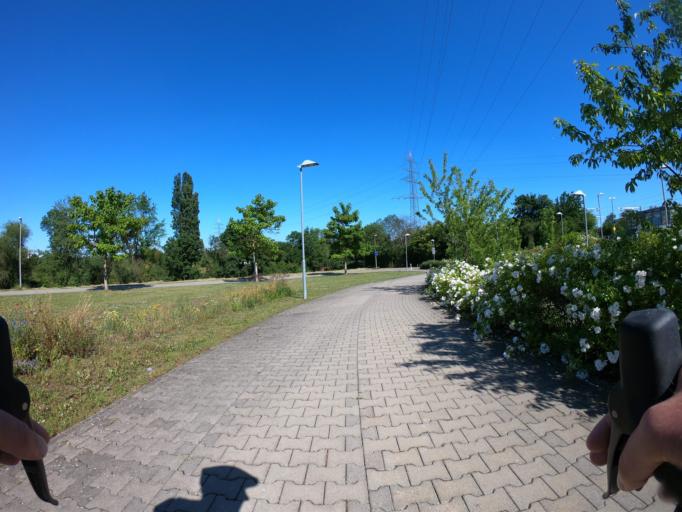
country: DE
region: Hesse
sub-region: Regierungsbezirk Darmstadt
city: Eschborn
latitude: 50.1340
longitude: 8.5783
